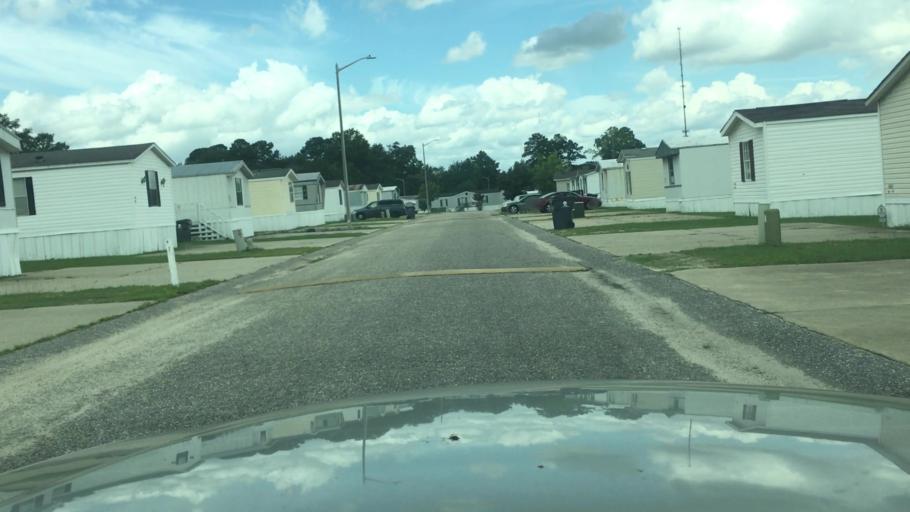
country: US
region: North Carolina
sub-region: Cumberland County
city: Hope Mills
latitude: 35.0390
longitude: -78.9792
